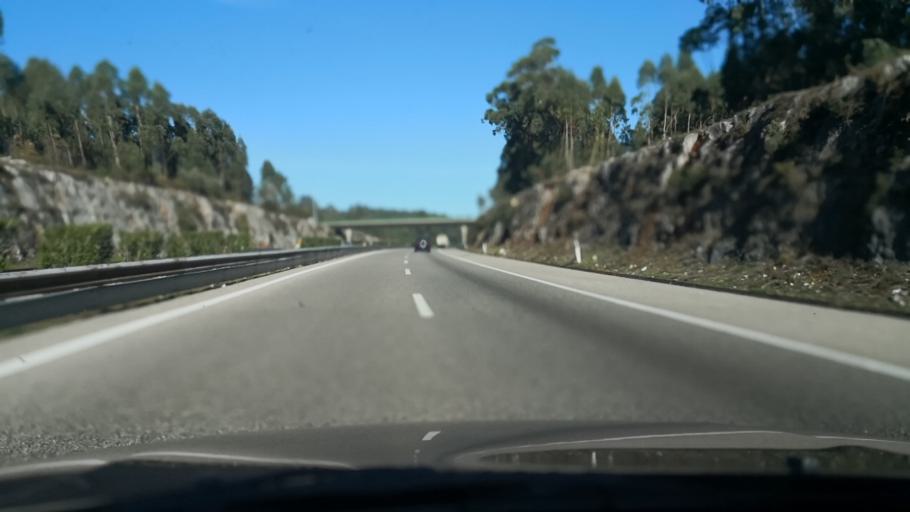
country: PT
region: Santarem
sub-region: Ourem
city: Fatima
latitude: 39.5451
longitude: -8.6620
